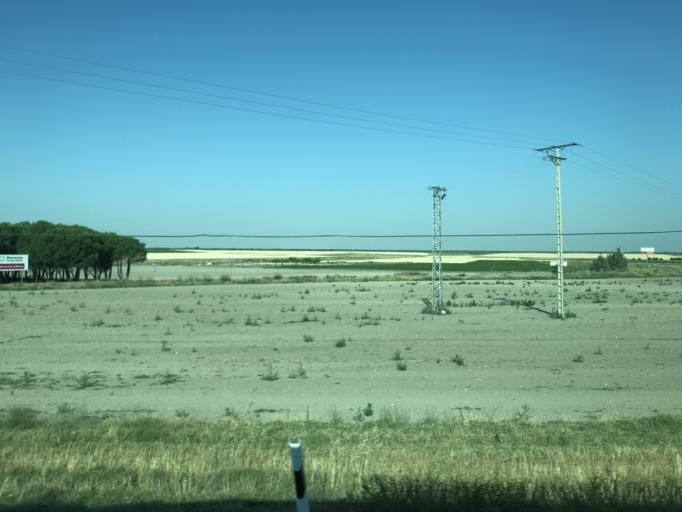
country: ES
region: Castille and Leon
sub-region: Provincia de Valladolid
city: Puras
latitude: 41.1904
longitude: -4.6610
